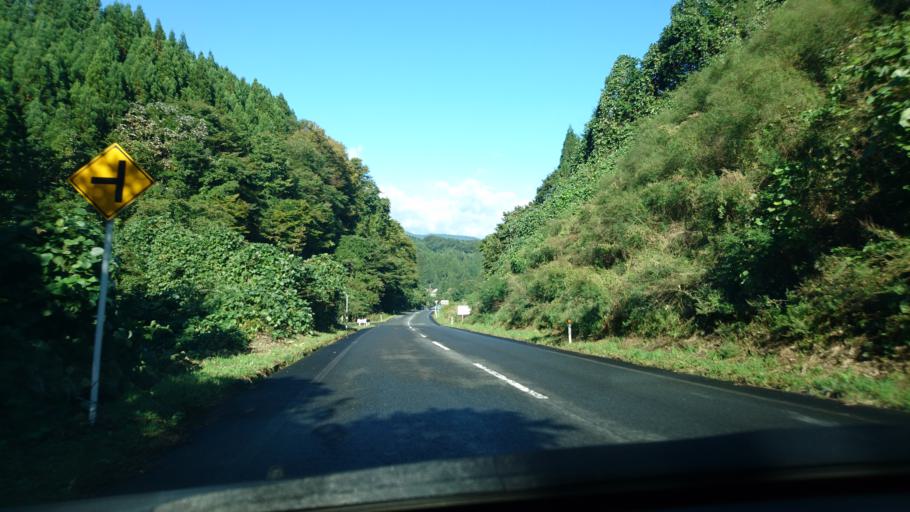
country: JP
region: Iwate
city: Ichinoseki
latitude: 39.0070
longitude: 141.0311
